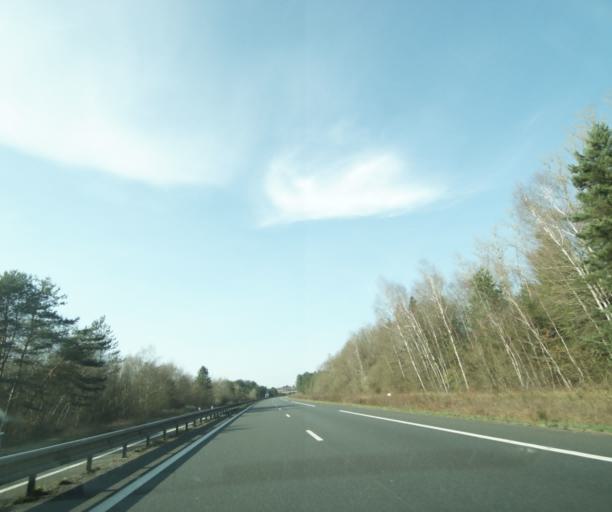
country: FR
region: Centre
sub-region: Departement du Loir-et-Cher
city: Lamotte-Beuvron
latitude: 47.6056
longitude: 1.9711
